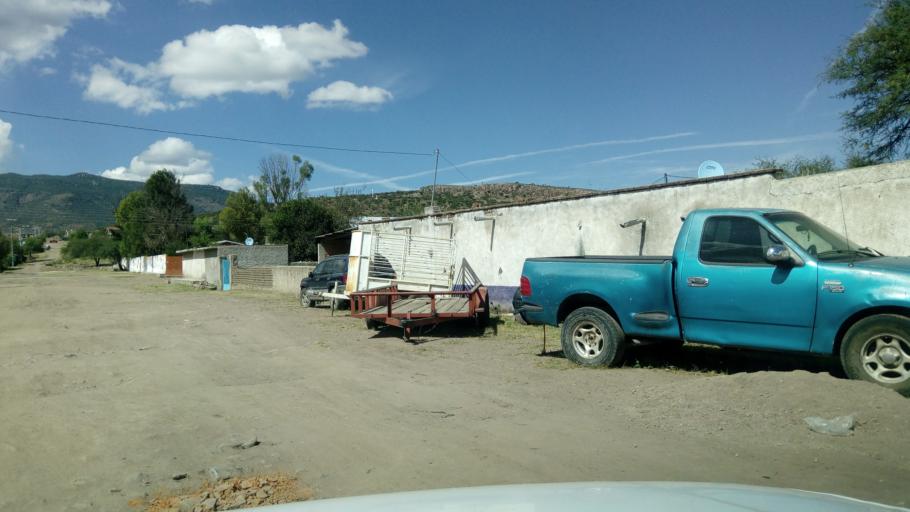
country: MX
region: Durango
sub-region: Durango
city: Jose Refugio Salcido
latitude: 23.7912
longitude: -104.4869
